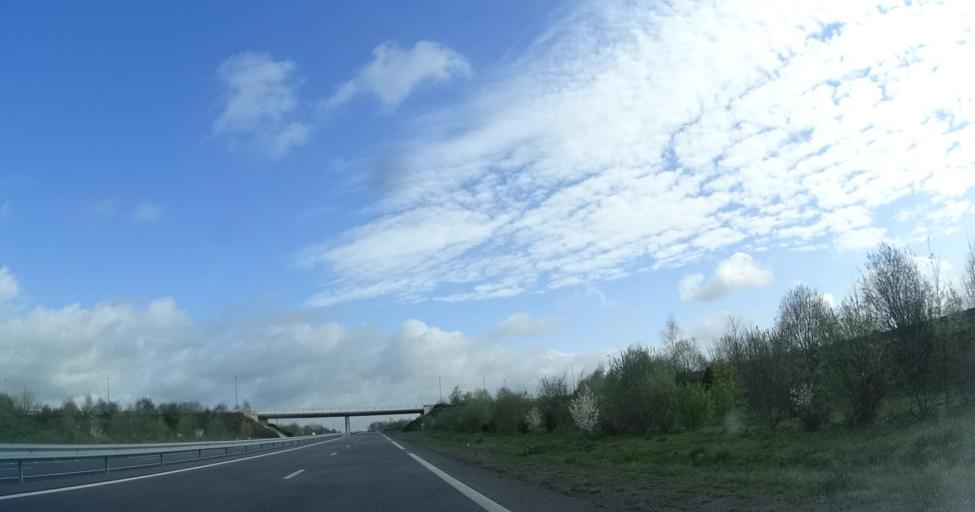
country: FR
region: Brittany
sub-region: Departement d'Ille-et-Vilaine
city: Pipriac
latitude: 47.8342
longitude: -1.9064
